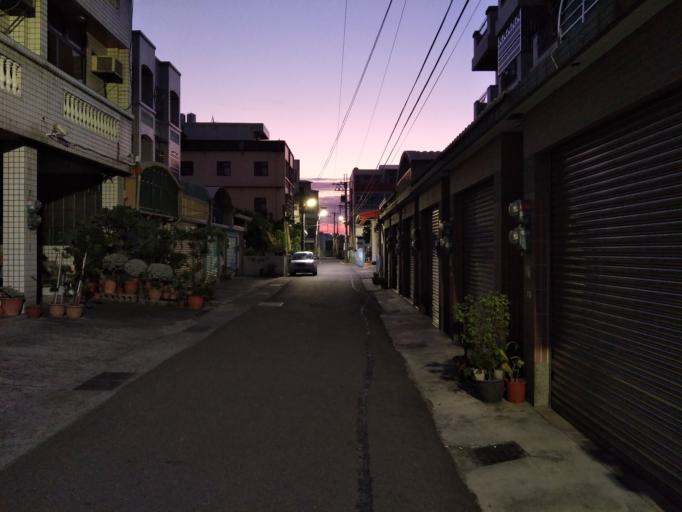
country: TW
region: Taiwan
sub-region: Changhua
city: Chang-hua
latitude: 23.9461
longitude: 120.5250
